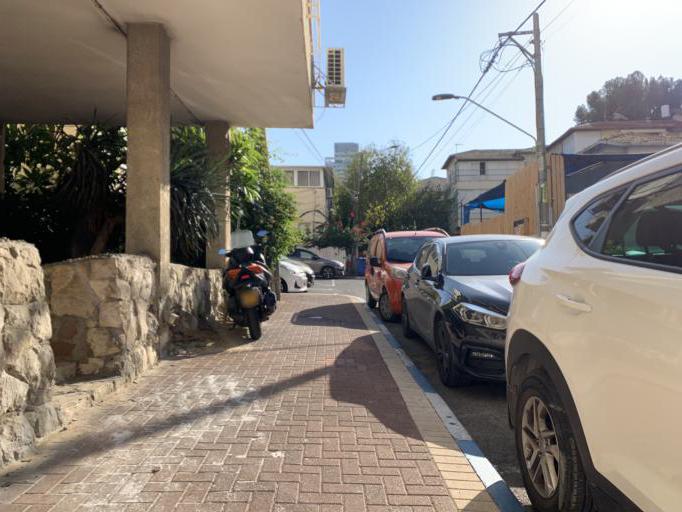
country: IL
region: Tel Aviv
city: Ramat Gan
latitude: 32.0877
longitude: 34.8069
